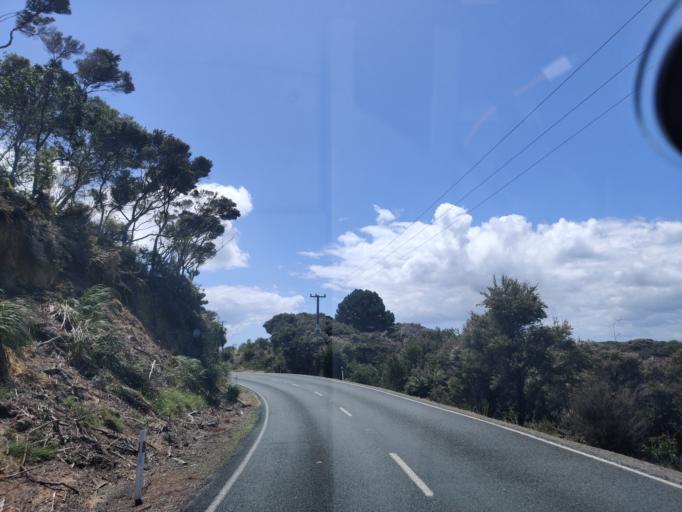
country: NZ
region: Northland
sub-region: Far North District
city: Kaitaia
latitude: -35.0239
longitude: 173.2133
